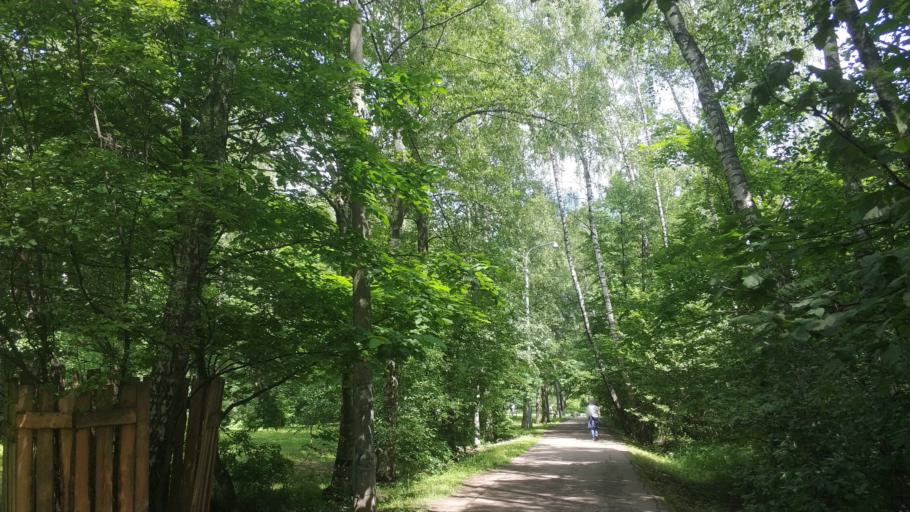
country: RU
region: Moscow
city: Perovo
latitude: 55.7294
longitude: 37.8018
